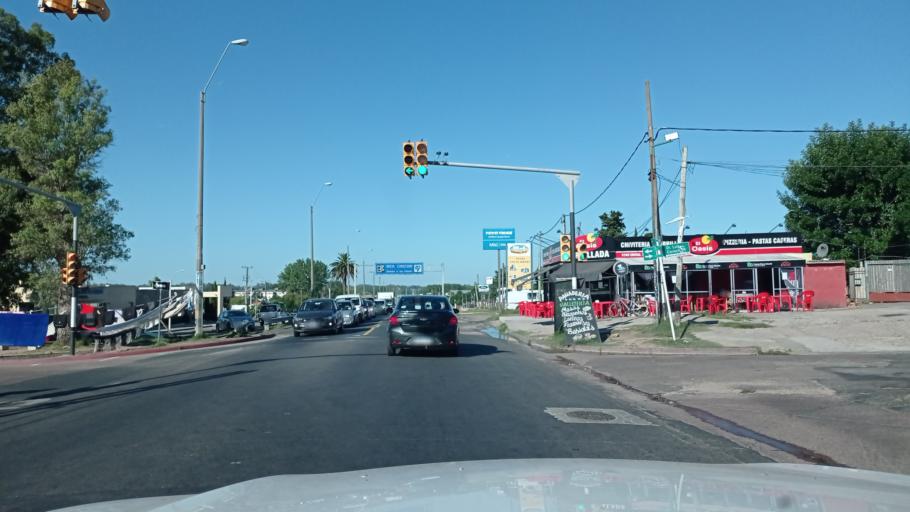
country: UY
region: Canelones
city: Pando
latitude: -34.7216
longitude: -55.9555
